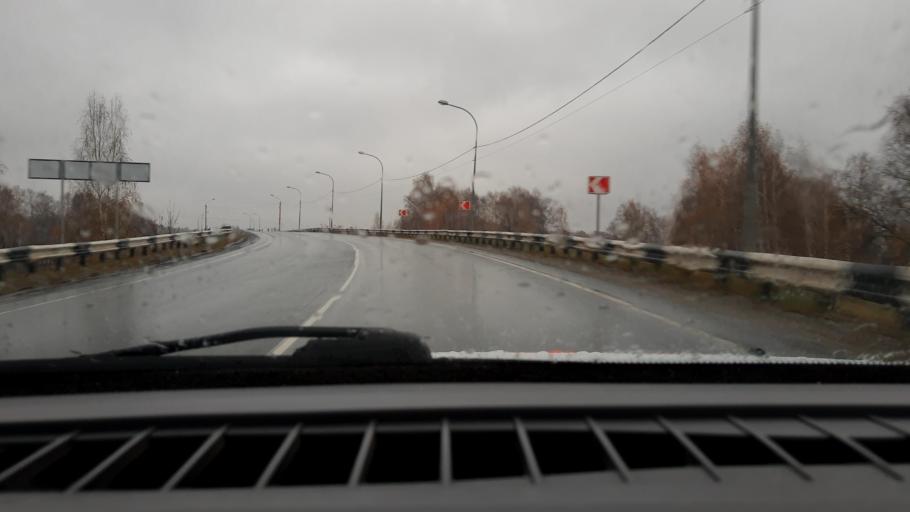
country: RU
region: Nizjnij Novgorod
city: Sitniki
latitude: 56.4669
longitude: 44.0373
